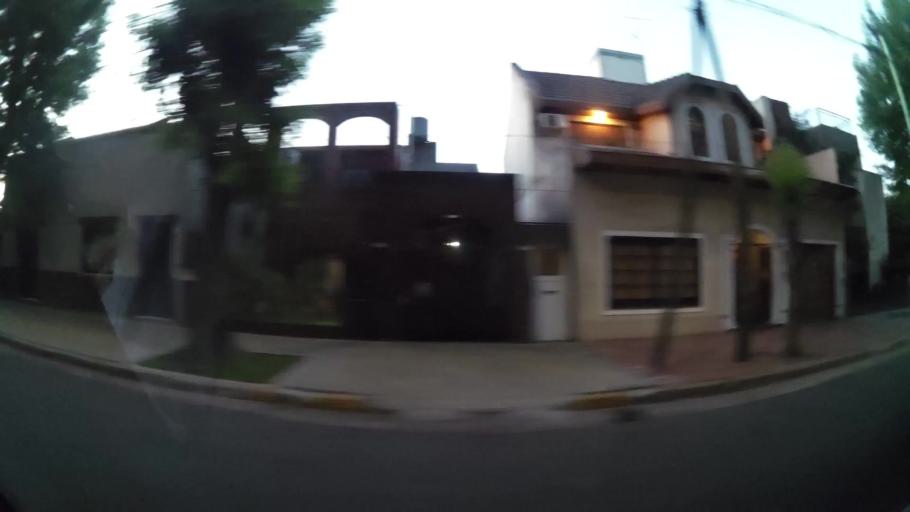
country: AR
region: Buenos Aires F.D.
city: Villa Lugano
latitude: -34.6802
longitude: -58.4788
